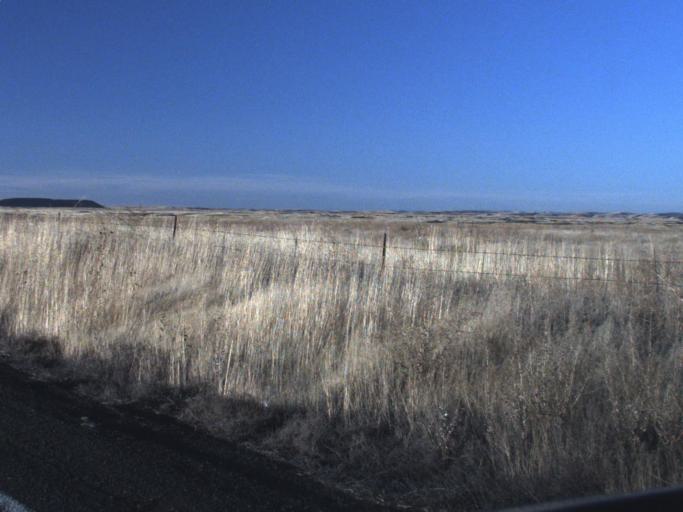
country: US
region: Washington
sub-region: Walla Walla County
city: Waitsburg
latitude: 46.6624
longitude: -118.2730
